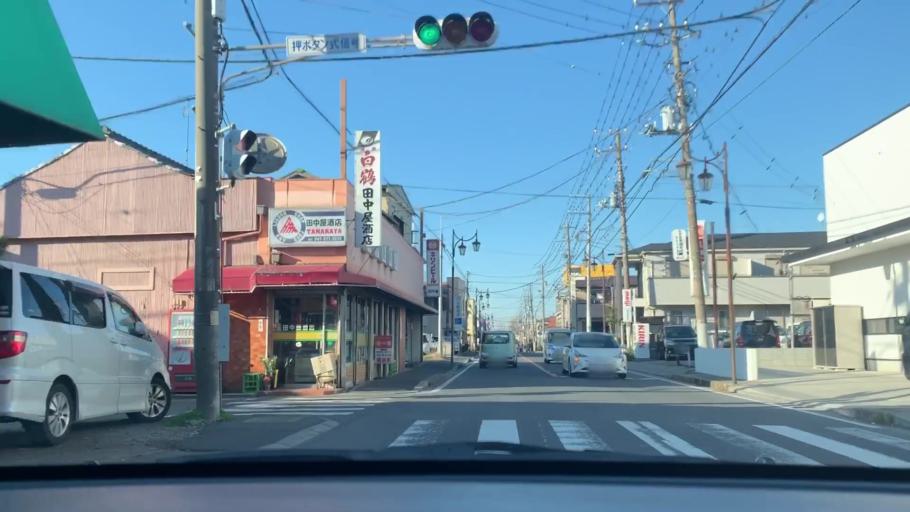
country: JP
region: Chiba
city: Matsudo
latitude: 35.7495
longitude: 139.9035
